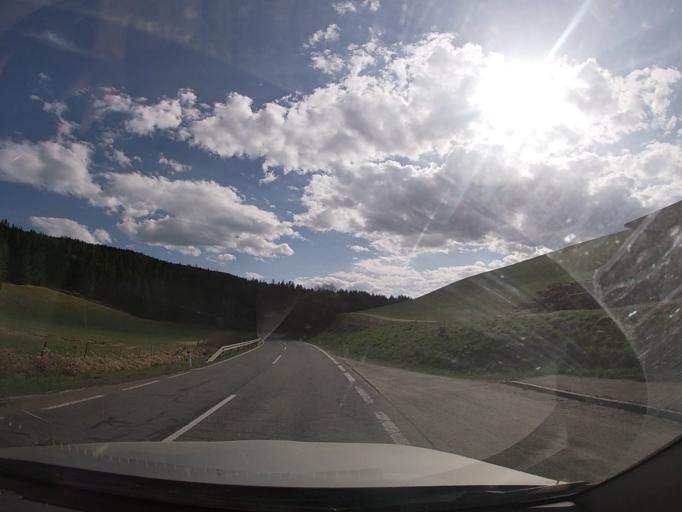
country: AT
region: Styria
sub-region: Politischer Bezirk Murau
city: Perchau am Sattel
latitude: 47.0964
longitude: 14.4498
